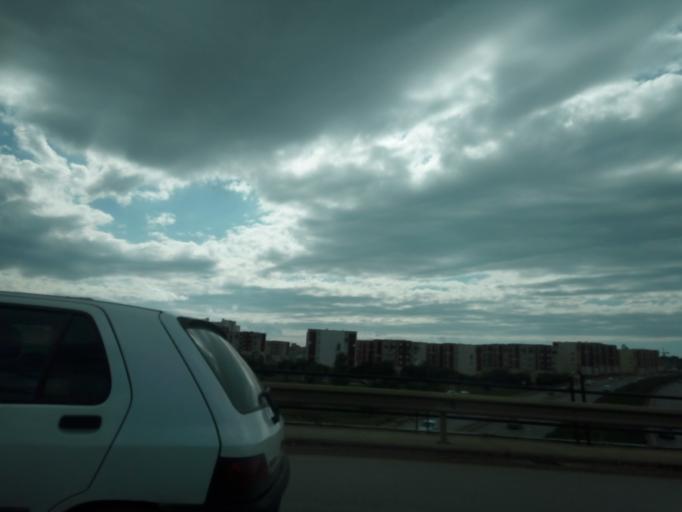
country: DZ
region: Tipaza
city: Douera
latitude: 36.6849
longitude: 2.9569
